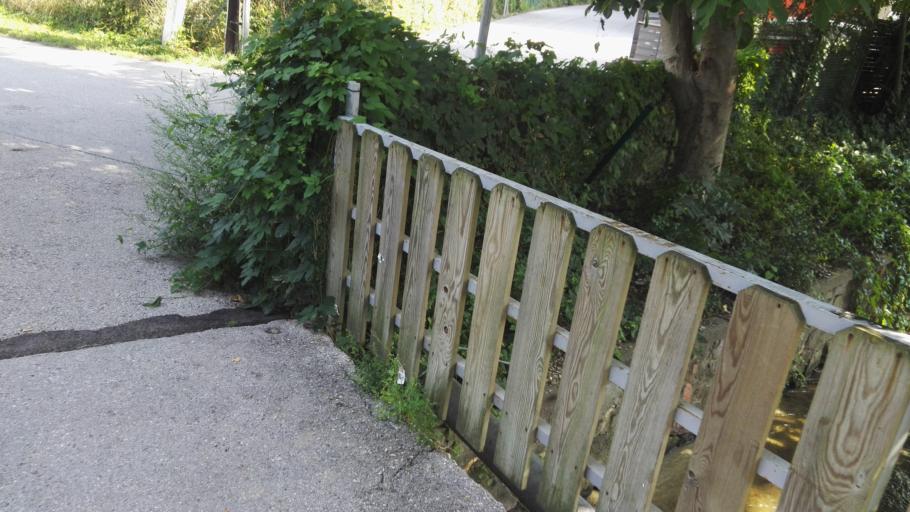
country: AT
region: Styria
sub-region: Graz Stadt
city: Goesting
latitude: 47.0932
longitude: 15.4114
